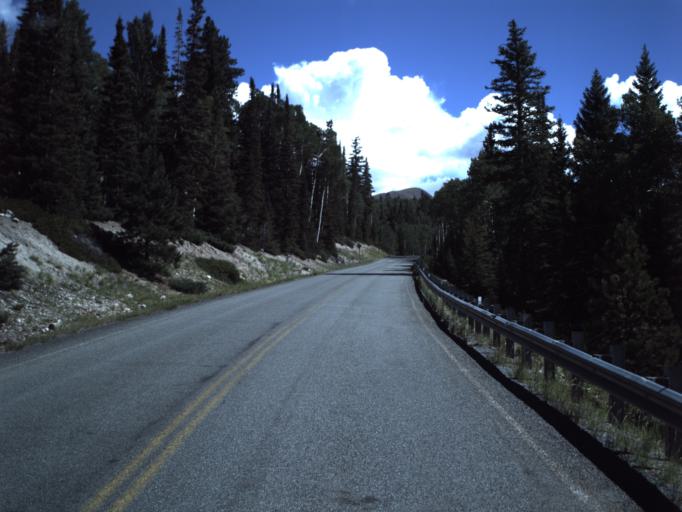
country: US
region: Utah
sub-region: Piute County
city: Junction
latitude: 38.3191
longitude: -112.3879
